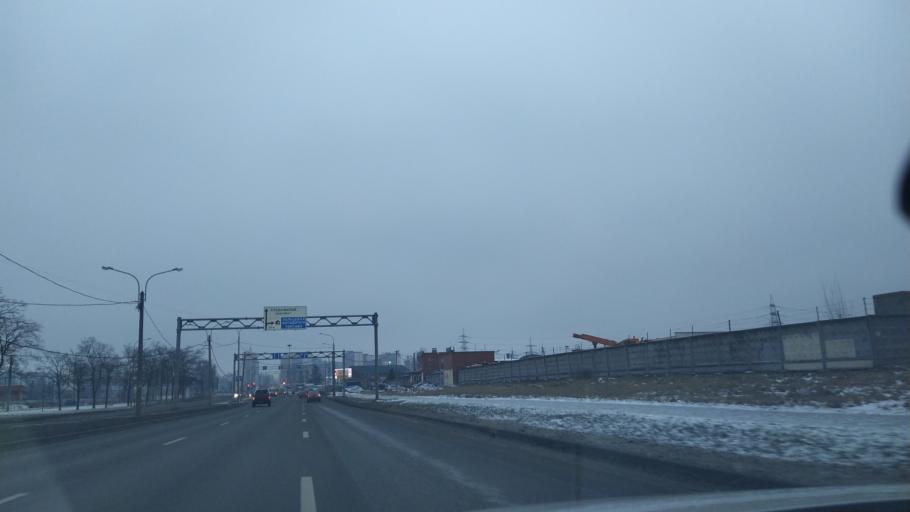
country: RU
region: Leningrad
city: Murino
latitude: 60.0372
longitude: 30.4327
